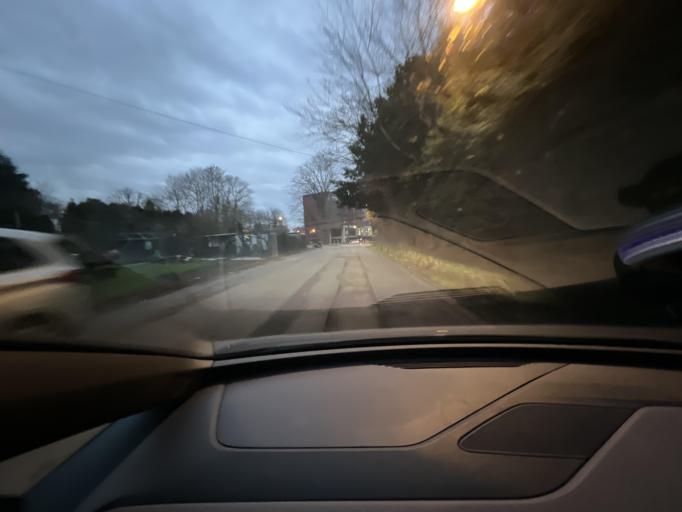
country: DE
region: Hesse
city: Sulzbach
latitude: 50.1079
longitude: 8.5561
